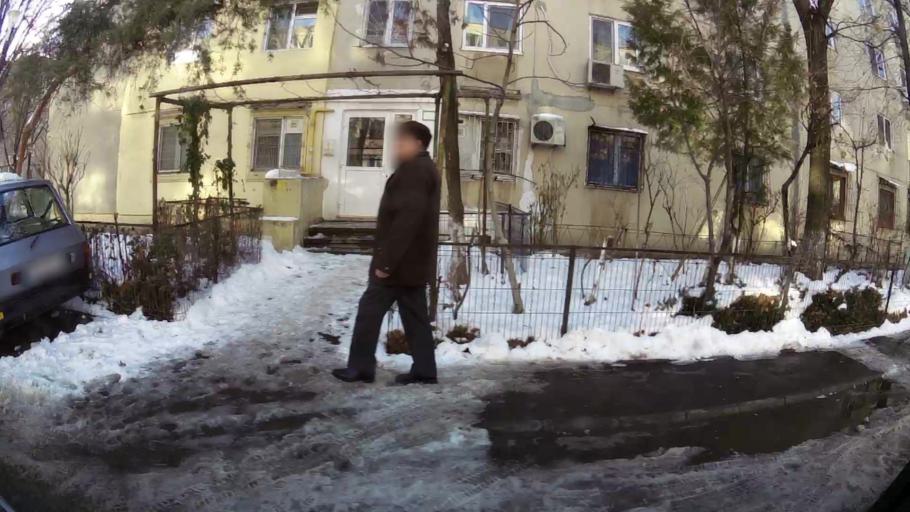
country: RO
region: Bucuresti
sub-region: Municipiul Bucuresti
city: Bucuresti
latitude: 44.3864
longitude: 26.0959
